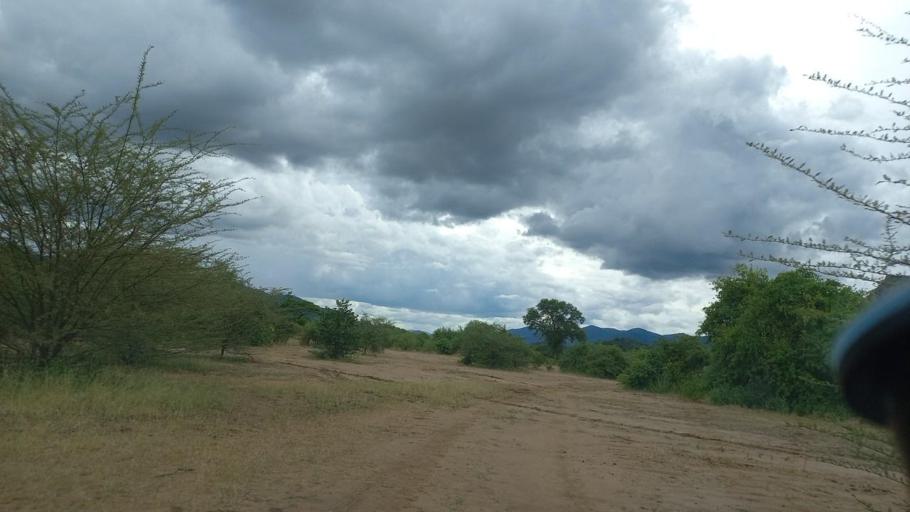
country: ZM
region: Lusaka
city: Luangwa
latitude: -15.6175
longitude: 30.2707
